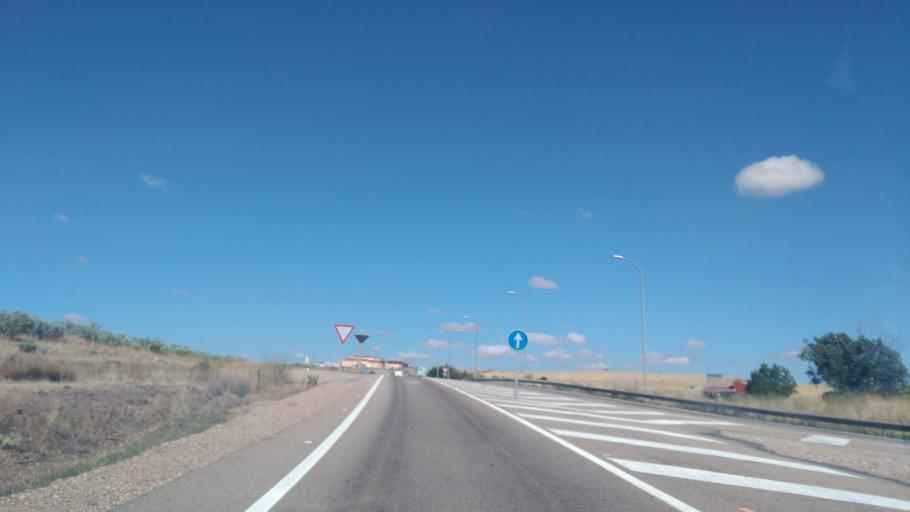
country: ES
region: Castille and Leon
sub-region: Provincia de Salamanca
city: Doninos de Salamanca
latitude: 40.9571
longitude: -5.7129
